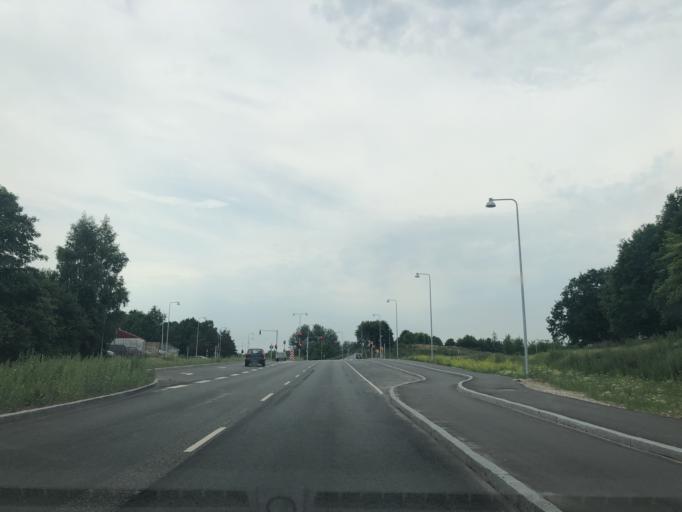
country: DK
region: Zealand
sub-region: Koge Kommune
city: Koge
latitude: 55.4759
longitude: 12.1701
